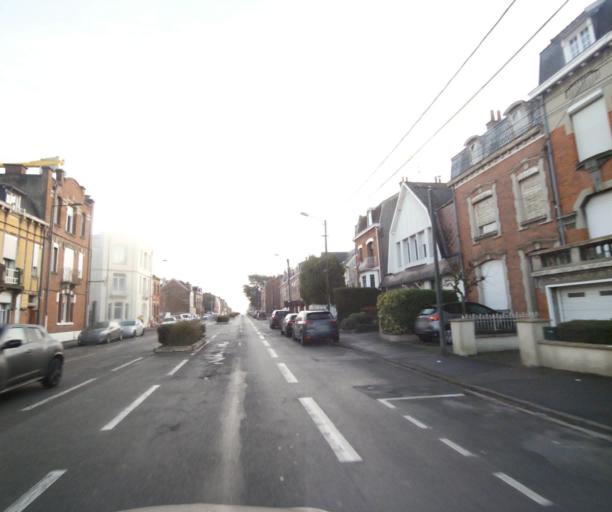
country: FR
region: Nord-Pas-de-Calais
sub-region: Departement du Nord
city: Valenciennes
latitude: 50.3645
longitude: 3.5384
